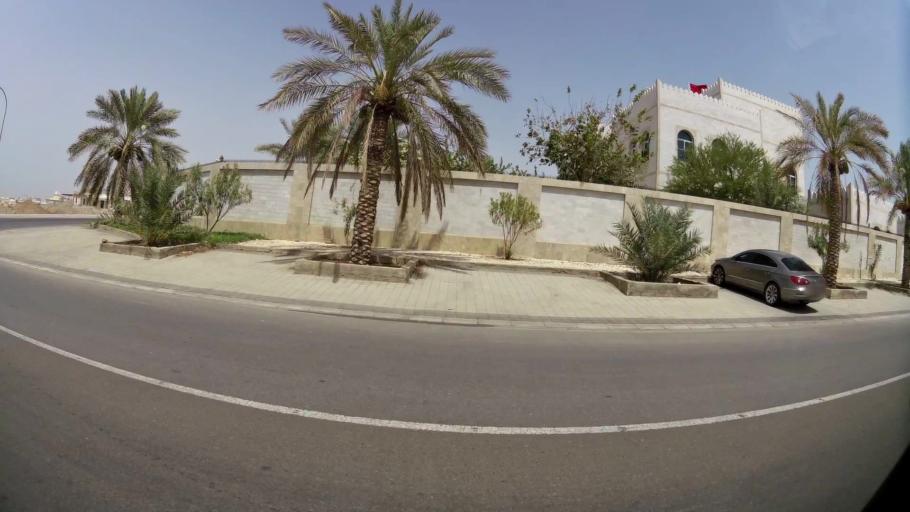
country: OM
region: Muhafazat Masqat
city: Bawshar
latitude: 23.5617
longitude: 58.3948
